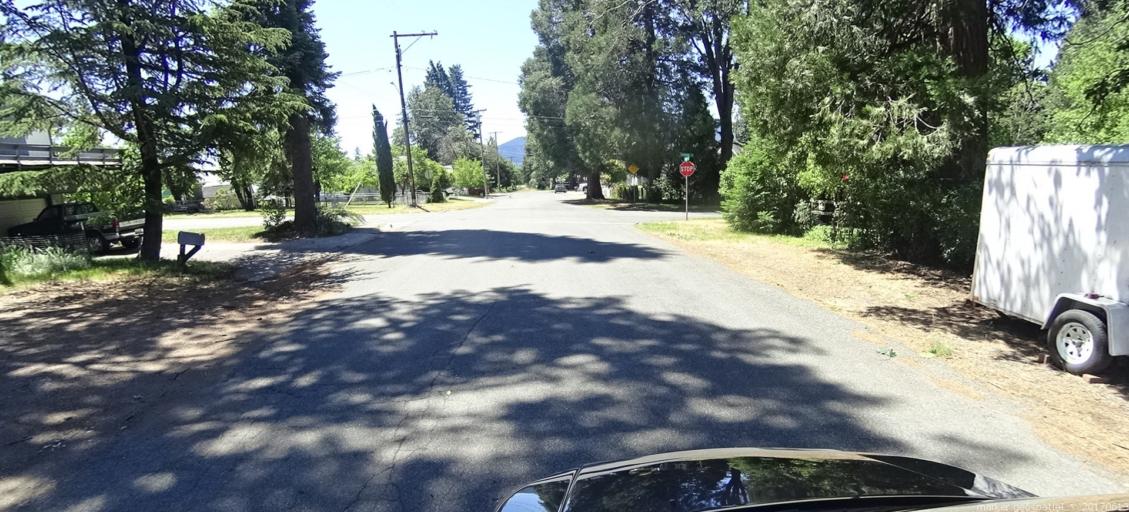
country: US
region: California
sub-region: Siskiyou County
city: Mount Shasta
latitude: 41.3080
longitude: -122.3124
